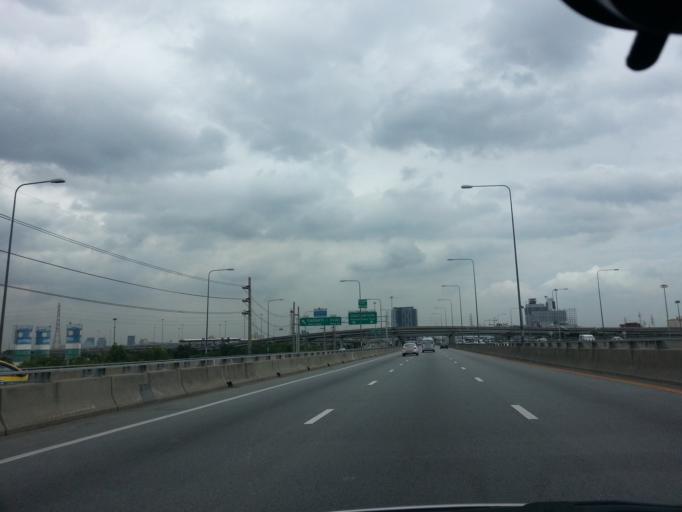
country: TH
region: Bangkok
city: Watthana
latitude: 13.7526
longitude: 100.5906
